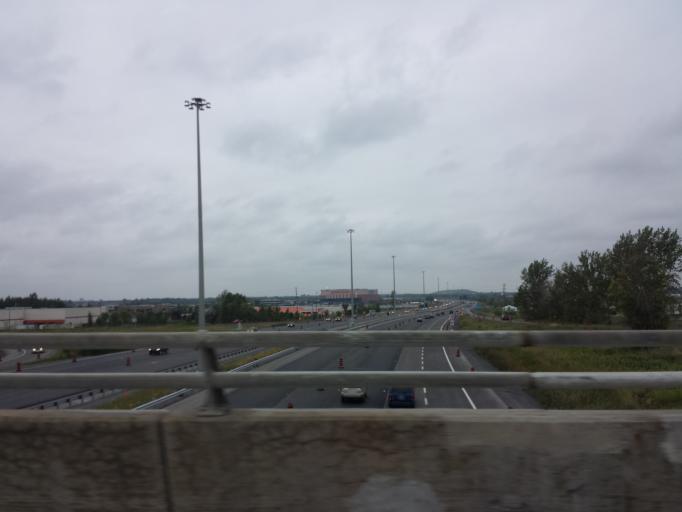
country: CA
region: Ontario
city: Bells Corners
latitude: 45.3057
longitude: -75.9119
